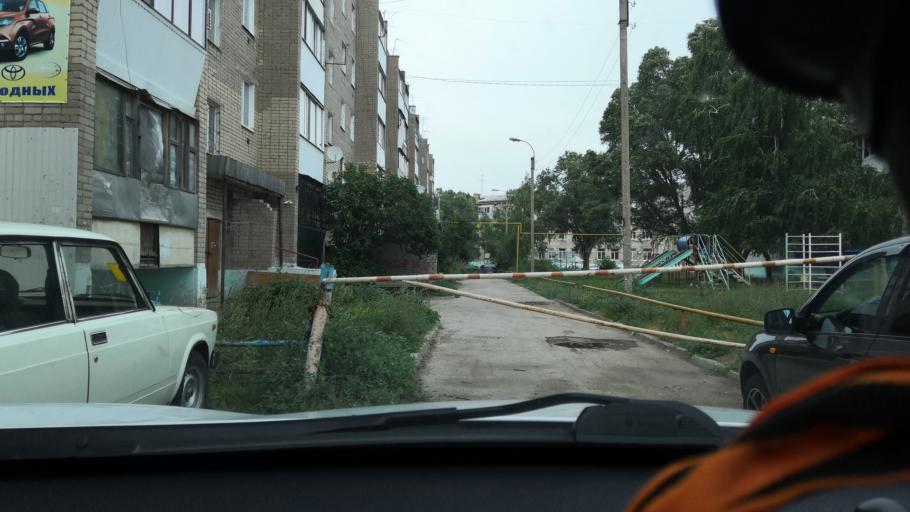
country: RU
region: Samara
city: Novosemeykino
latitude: 53.3712
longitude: 50.3523
